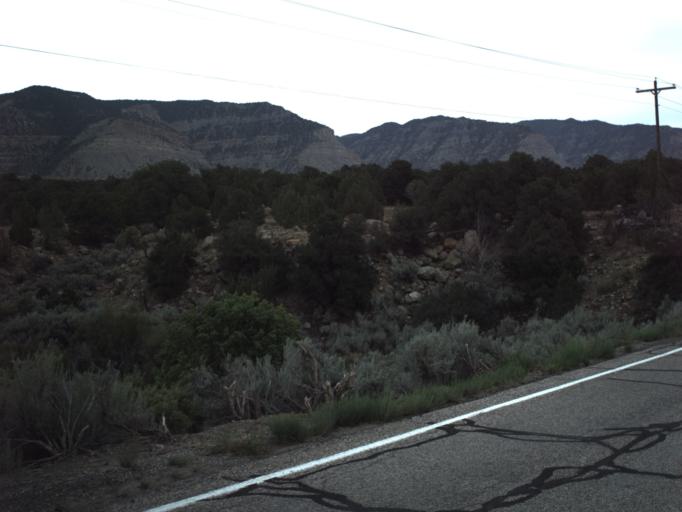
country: US
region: Utah
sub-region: Carbon County
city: East Carbon City
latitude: 39.5398
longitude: -110.4058
